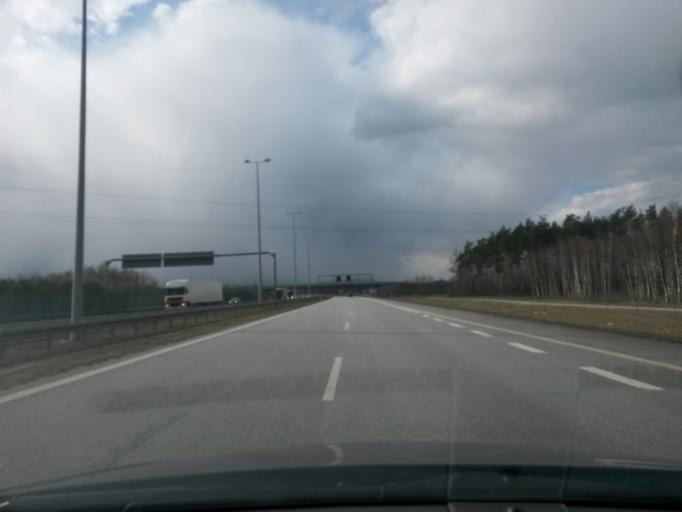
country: PL
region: Greater Poland Voivodeship
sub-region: Powiat koninski
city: Stare Miasto
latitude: 52.1578
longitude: 18.2598
